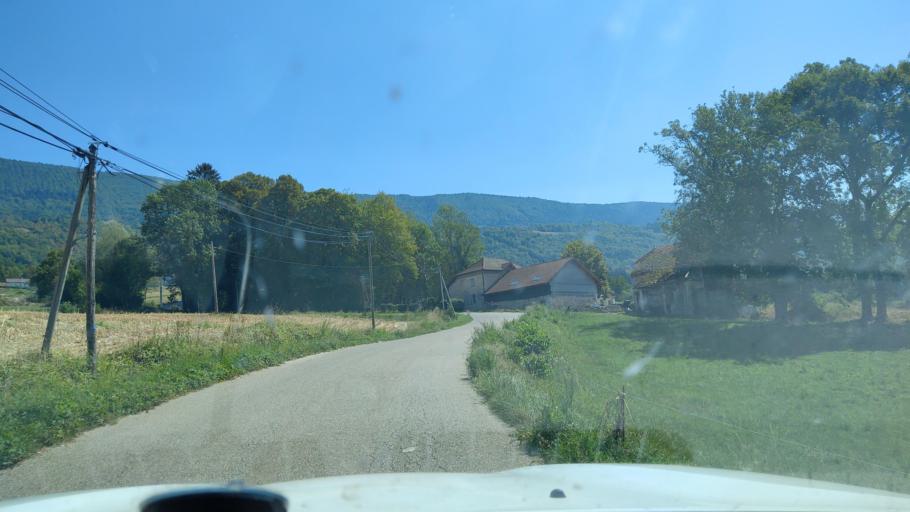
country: FR
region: Rhone-Alpes
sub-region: Departement de la Savoie
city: Novalaise
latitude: 45.6404
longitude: 5.7764
